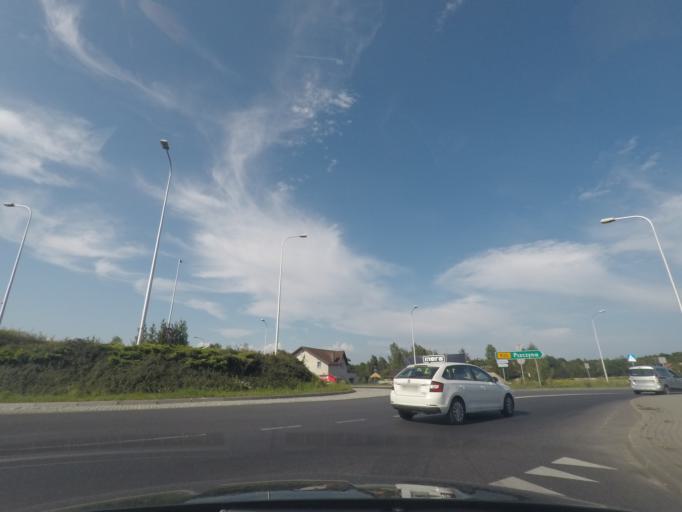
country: PL
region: Silesian Voivodeship
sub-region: Zory
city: Zory
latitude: 50.0583
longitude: 18.6826
